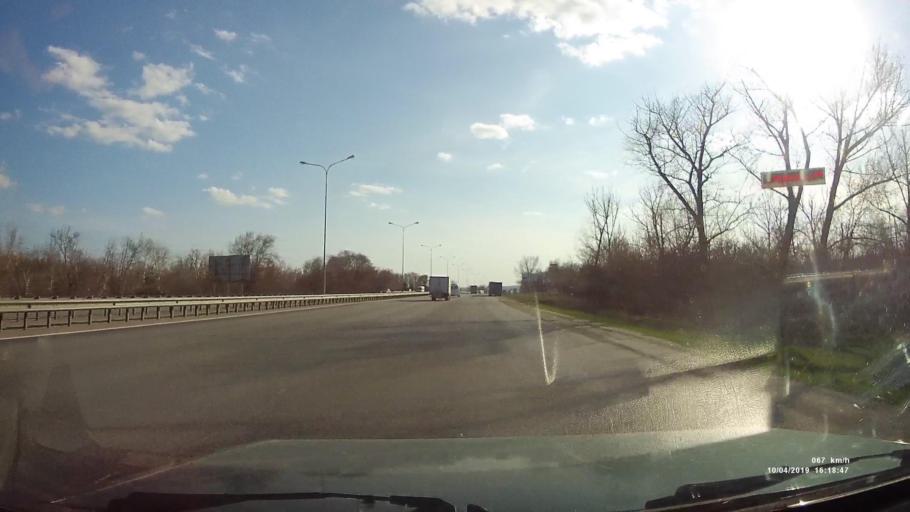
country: RU
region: Rostov
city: Staraya Stanitsa
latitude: 48.3191
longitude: 40.3300
